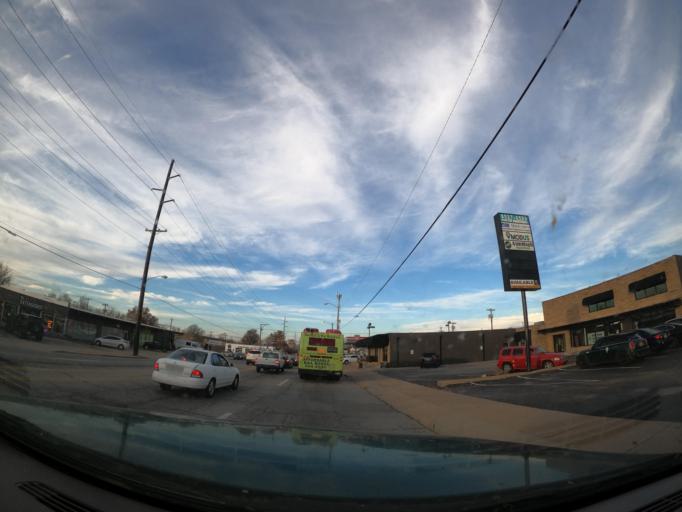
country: US
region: Oklahoma
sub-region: Tulsa County
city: Tulsa
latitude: 36.1396
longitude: -95.9402
